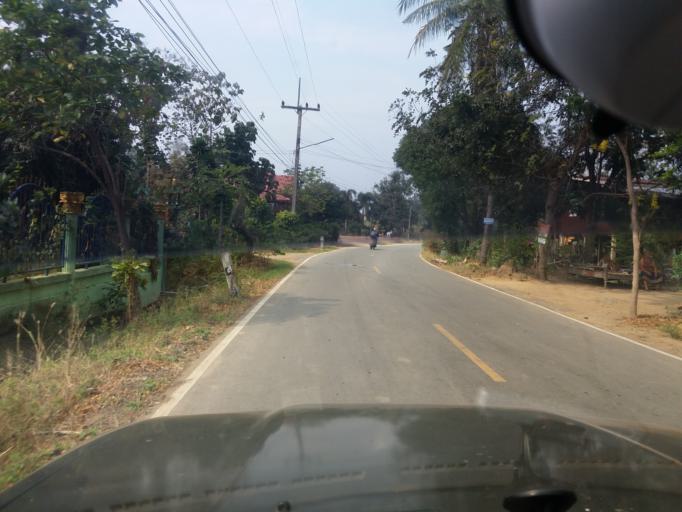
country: TH
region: Suphan Buri
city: Doem Bang Nang Buat
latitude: 14.8918
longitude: 100.1722
